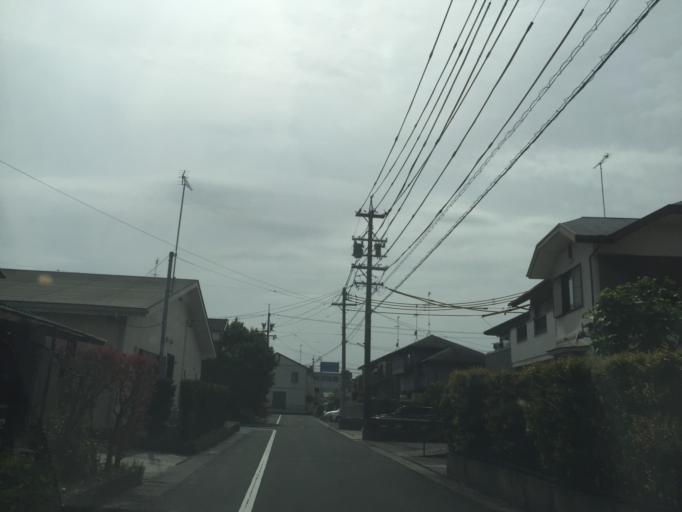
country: JP
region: Shizuoka
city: Kakegawa
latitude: 34.7797
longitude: 138.0155
